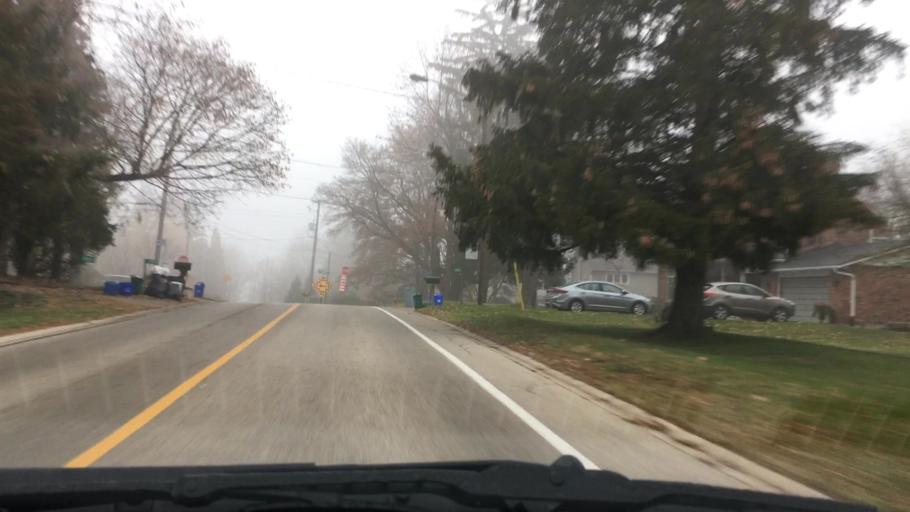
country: CA
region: Ontario
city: Burlington
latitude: 43.3245
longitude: -79.8893
